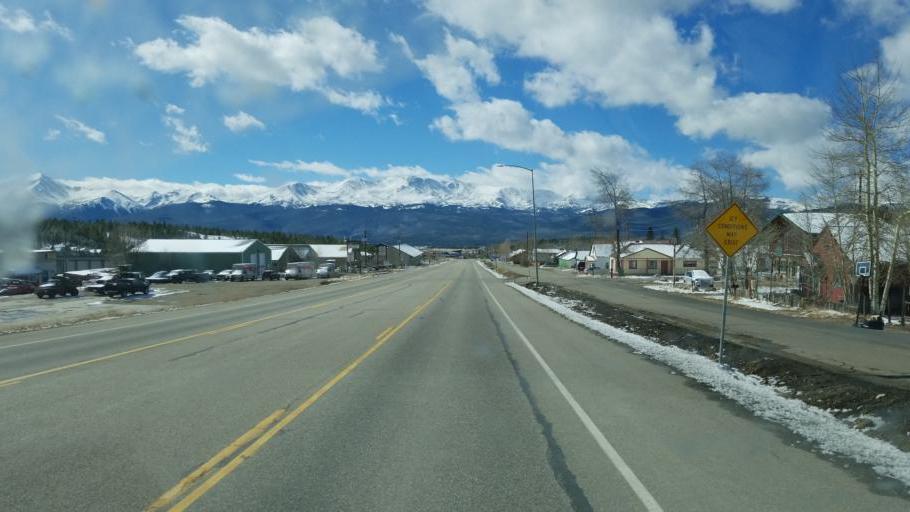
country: US
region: Colorado
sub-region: Lake County
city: Leadville
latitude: 39.2412
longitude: -106.2973
